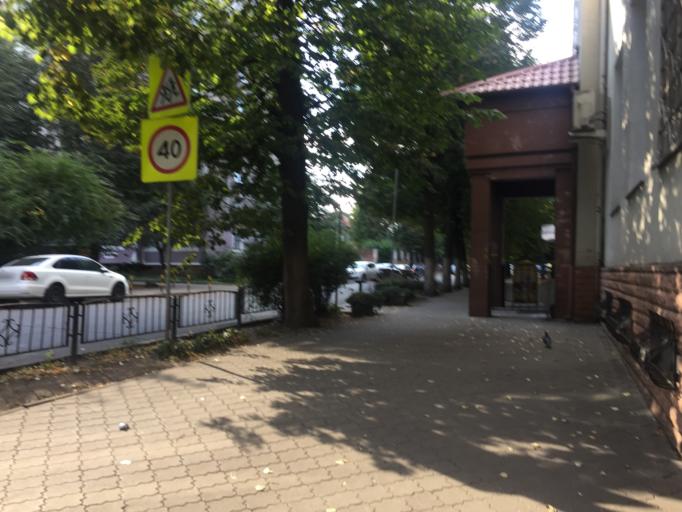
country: RU
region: Kaliningrad
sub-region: Gorod Kaliningrad
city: Kaliningrad
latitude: 54.6973
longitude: 20.5087
